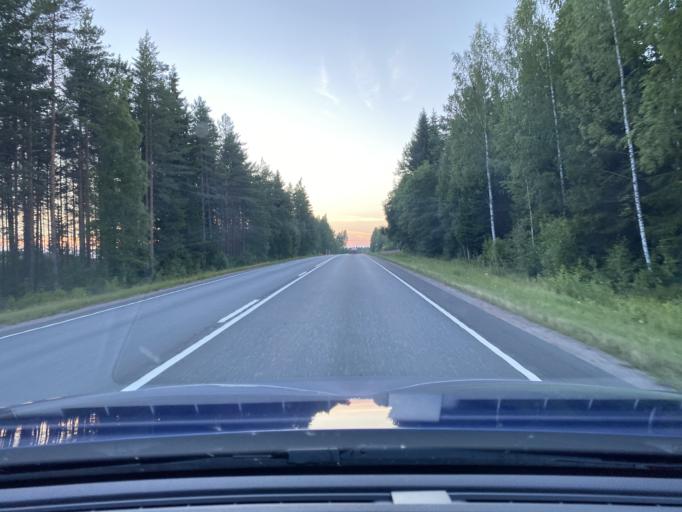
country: FI
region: Pirkanmaa
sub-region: Luoteis-Pirkanmaa
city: Ikaalinen
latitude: 61.8177
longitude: 22.9530
